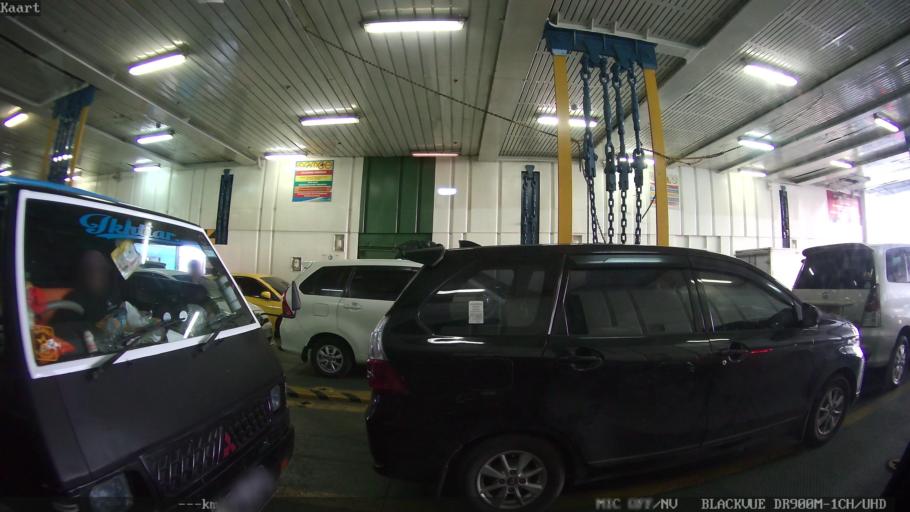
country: ID
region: Lampung
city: Penengahan
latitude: -5.8652
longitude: 105.7574
